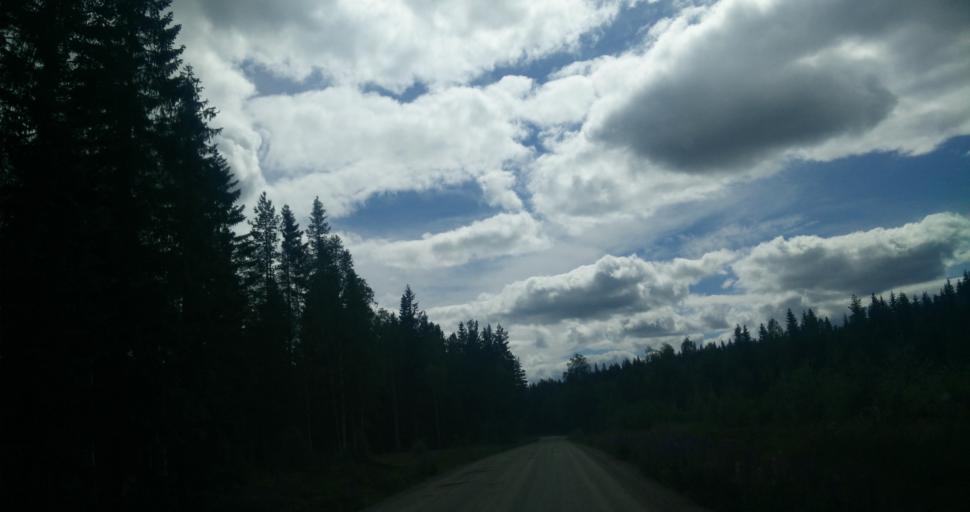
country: SE
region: Gaevleborg
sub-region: Nordanstigs Kommun
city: Bergsjoe
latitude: 62.1114
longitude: 17.0991
